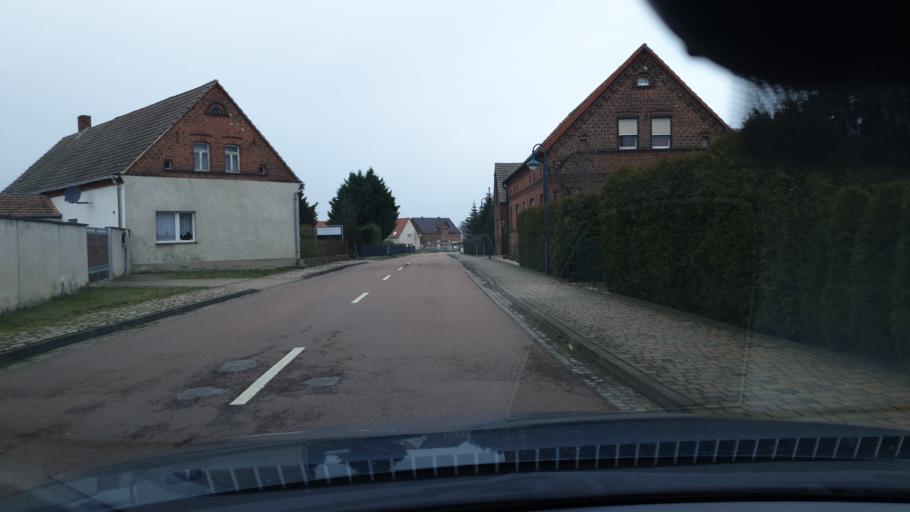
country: DE
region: Saxony-Anhalt
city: Radis
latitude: 51.7813
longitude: 12.4867
